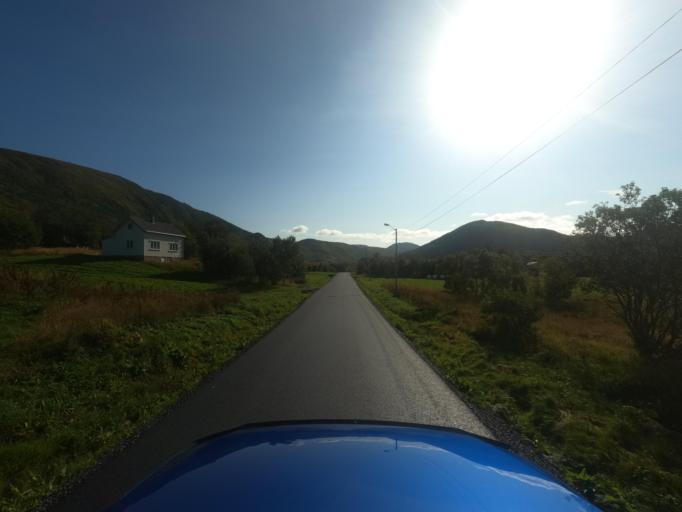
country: NO
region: Nordland
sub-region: Vestvagoy
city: Evjen
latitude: 68.2542
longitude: 13.8502
